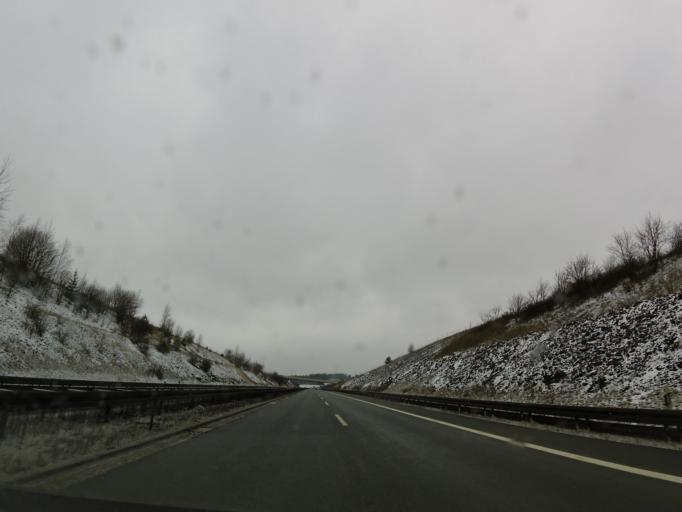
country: DE
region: Bavaria
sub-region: Upper Franconia
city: Gattendorf
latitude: 50.3452
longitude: 11.9923
